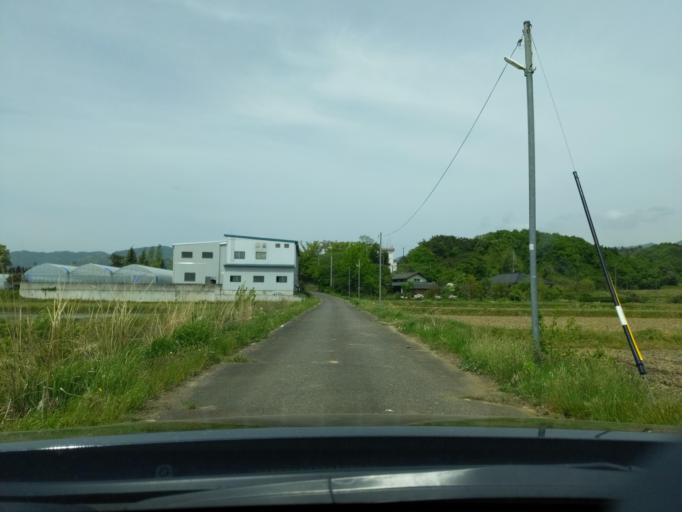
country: JP
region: Fukushima
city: Koriyama
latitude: 37.4060
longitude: 140.2748
